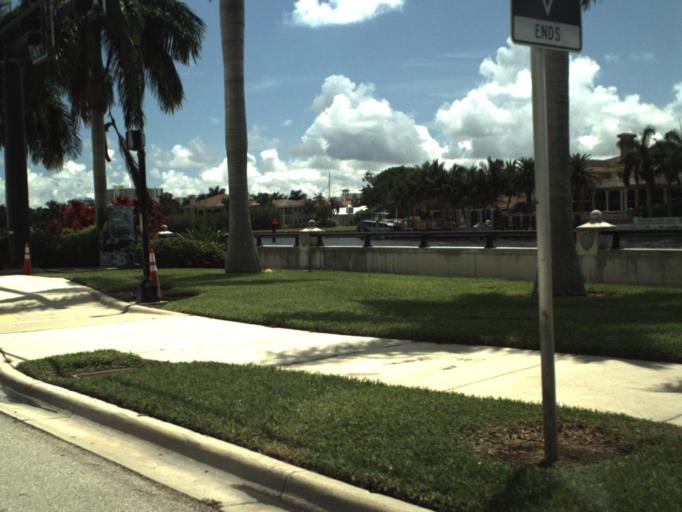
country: US
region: Florida
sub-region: Broward County
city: Hollywood
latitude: 26.0060
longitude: -80.1183
